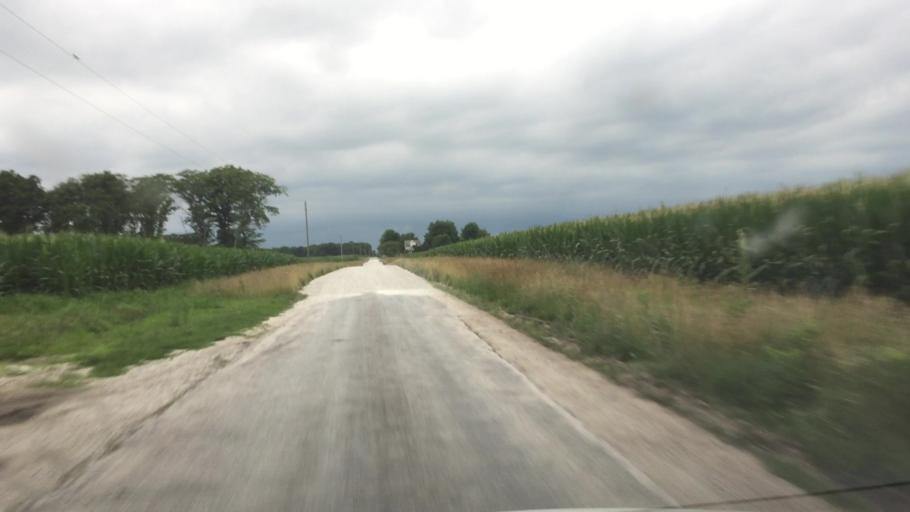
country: US
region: Illinois
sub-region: Adams County
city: Camp Point
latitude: 40.2156
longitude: -90.9645
